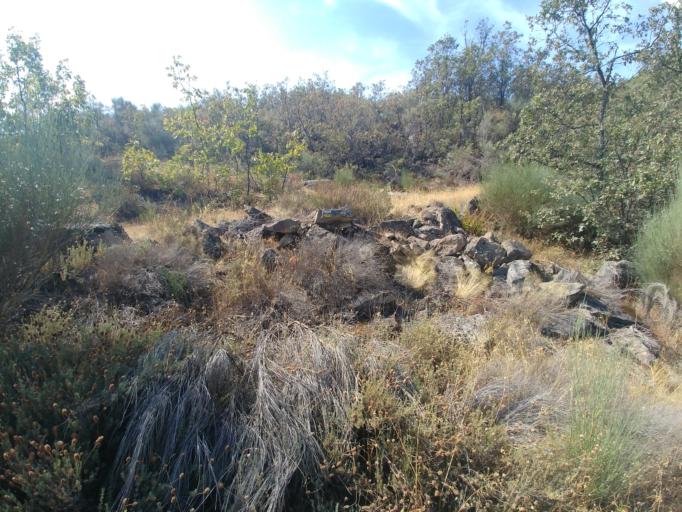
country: ES
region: Extremadura
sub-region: Provincia de Caceres
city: Garganta la Olla
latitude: 40.0954
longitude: -5.7535
